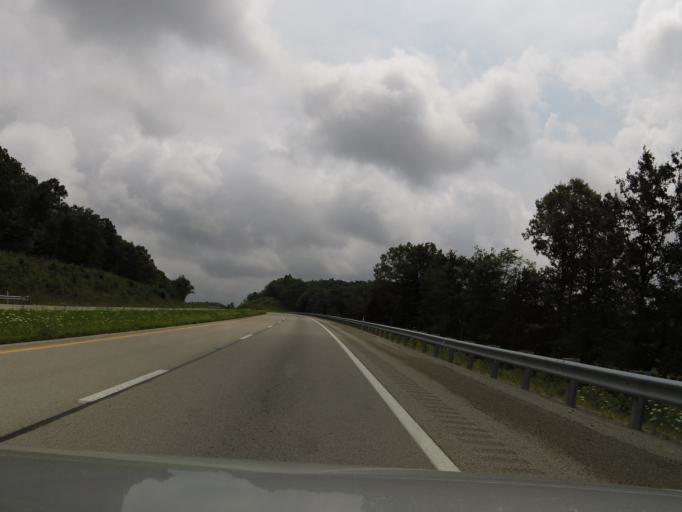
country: US
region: Kentucky
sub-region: Ohio County
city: Oak Grove
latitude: 37.3842
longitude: -86.6573
